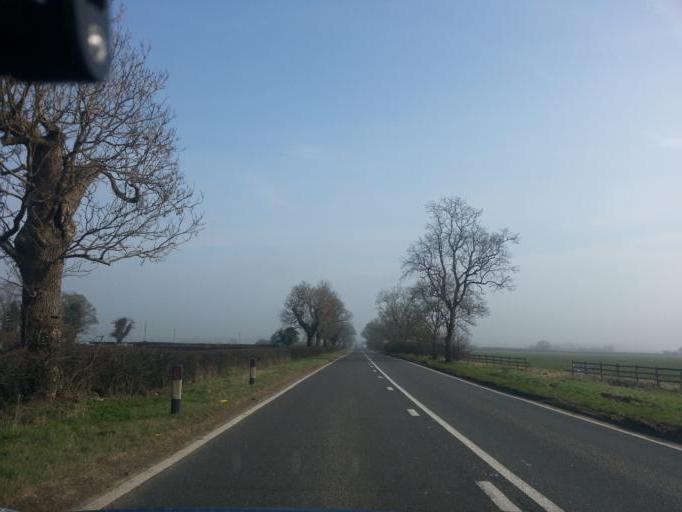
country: GB
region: England
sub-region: Oxfordshire
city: Shrivenham
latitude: 51.6239
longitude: -1.6254
